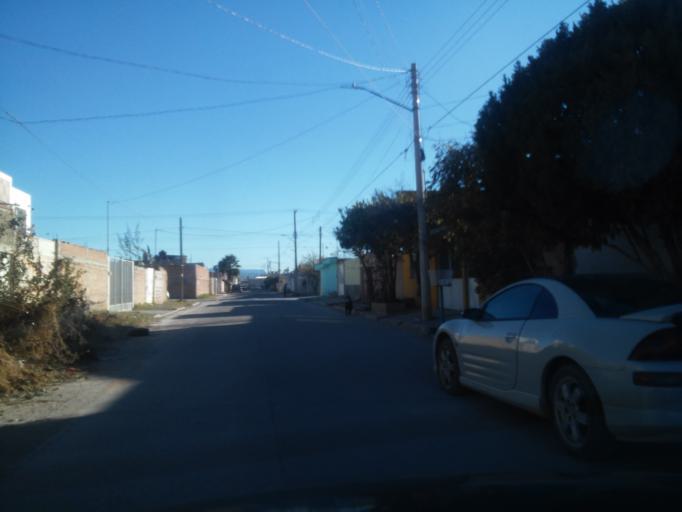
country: MX
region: Durango
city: Victoria de Durango
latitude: 24.0154
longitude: -104.6375
